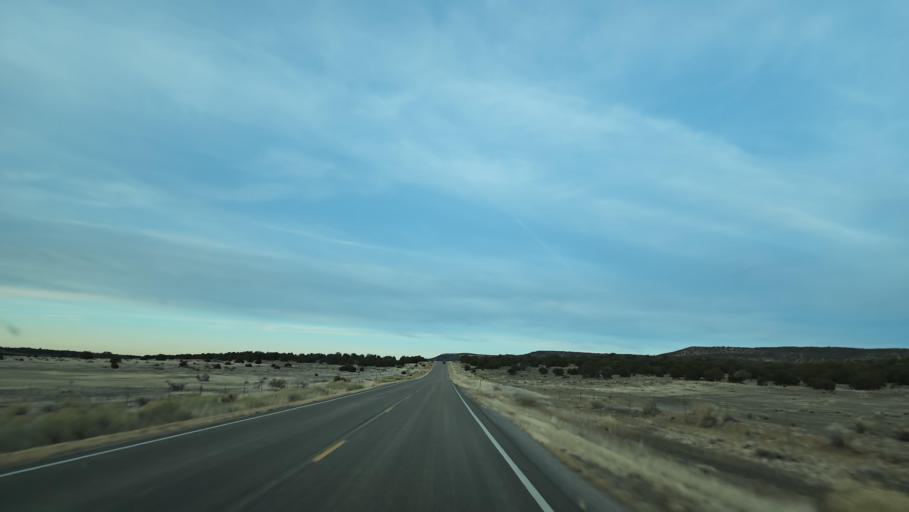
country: US
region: New Mexico
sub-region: Cibola County
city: Grants
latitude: 34.7179
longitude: -107.9826
